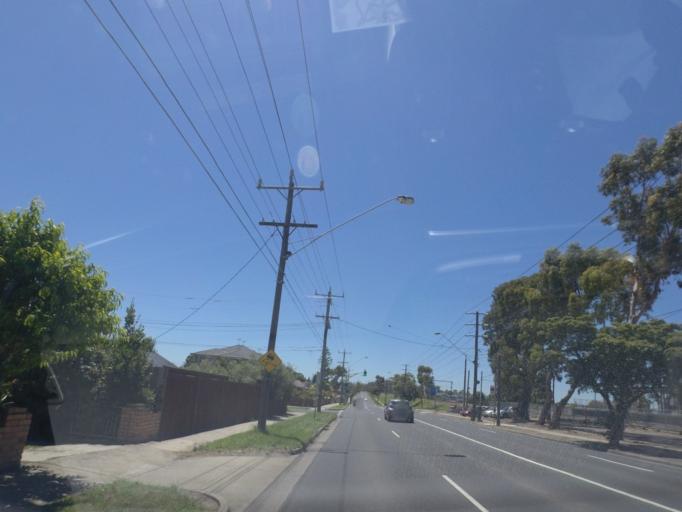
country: AU
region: Victoria
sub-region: Darebin
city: Reservoir
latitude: -37.7082
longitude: 145.0090
